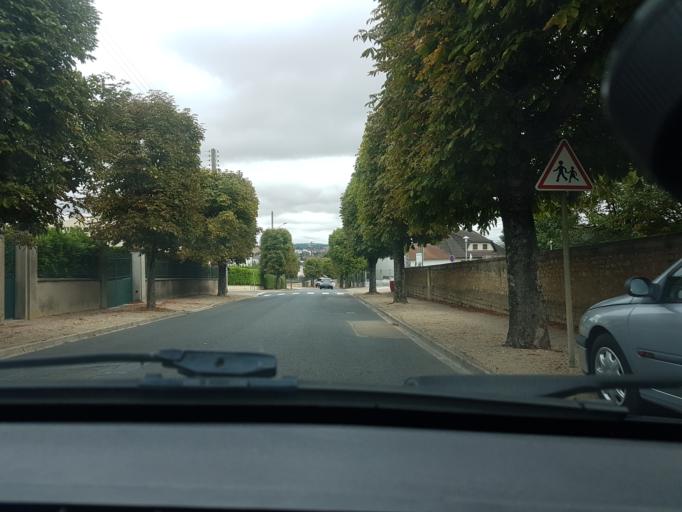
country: FR
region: Bourgogne
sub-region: Departement de l'Yonne
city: Auxerre
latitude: 47.8052
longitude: 3.5709
